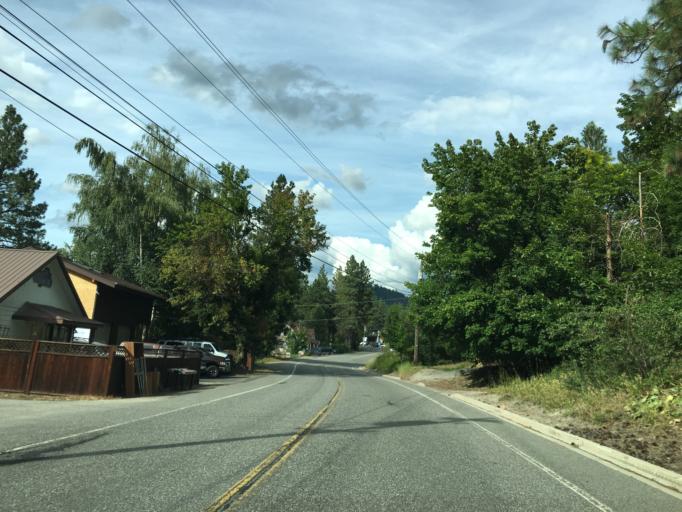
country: US
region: Washington
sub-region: Chelan County
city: Leavenworth
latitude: 47.5964
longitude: -120.6520
